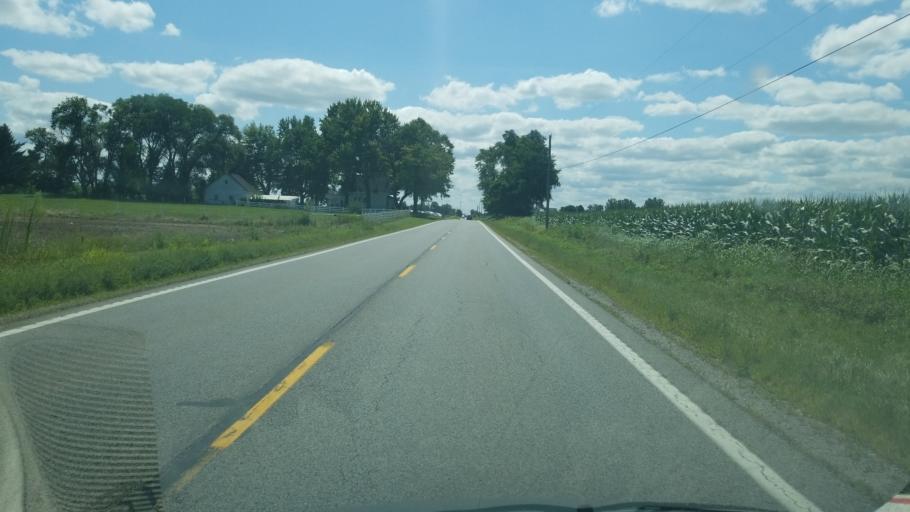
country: US
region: Ohio
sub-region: Fulton County
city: Delta
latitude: 41.6119
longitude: -84.0375
